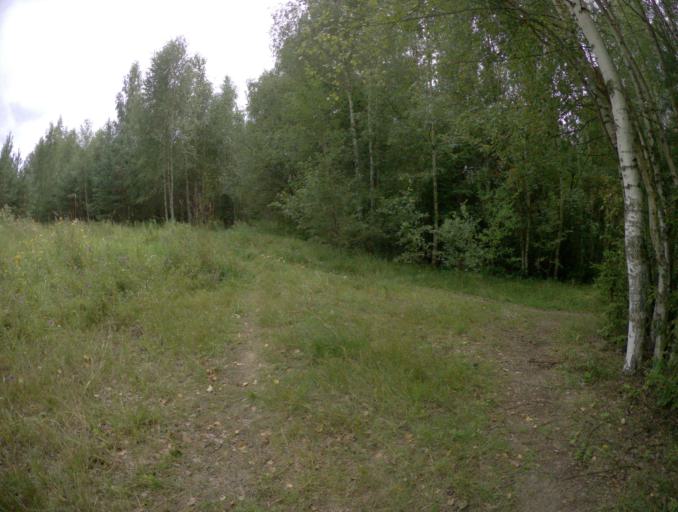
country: RU
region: Vladimir
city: Raduzhnyy
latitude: 56.0045
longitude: 40.3197
